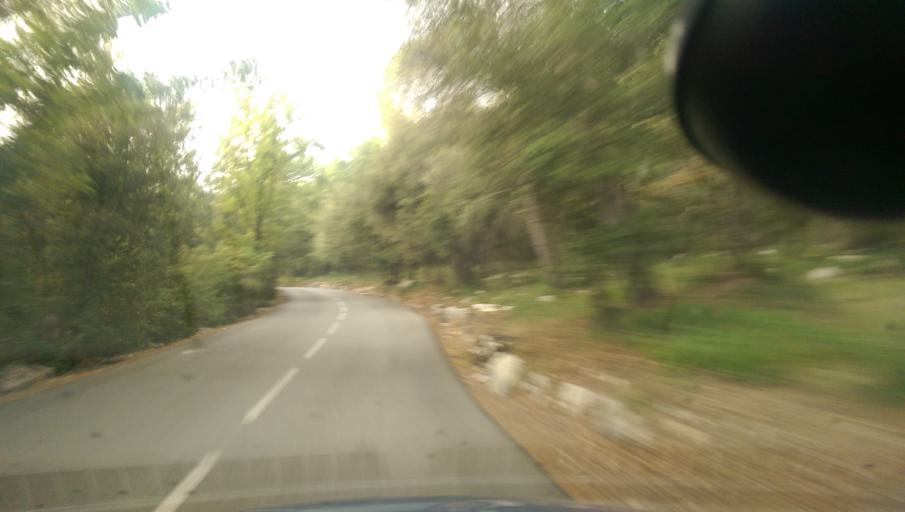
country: FR
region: Provence-Alpes-Cote d'Azur
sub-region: Departement des Alpes-Maritimes
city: Valbonne
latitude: 43.6392
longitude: 7.0437
